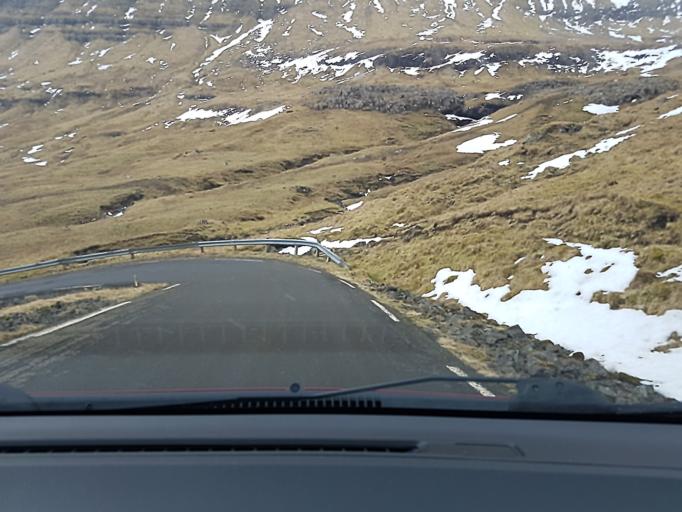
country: FO
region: Streymoy
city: Kollafjordhur
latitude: 62.0468
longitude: -6.9226
